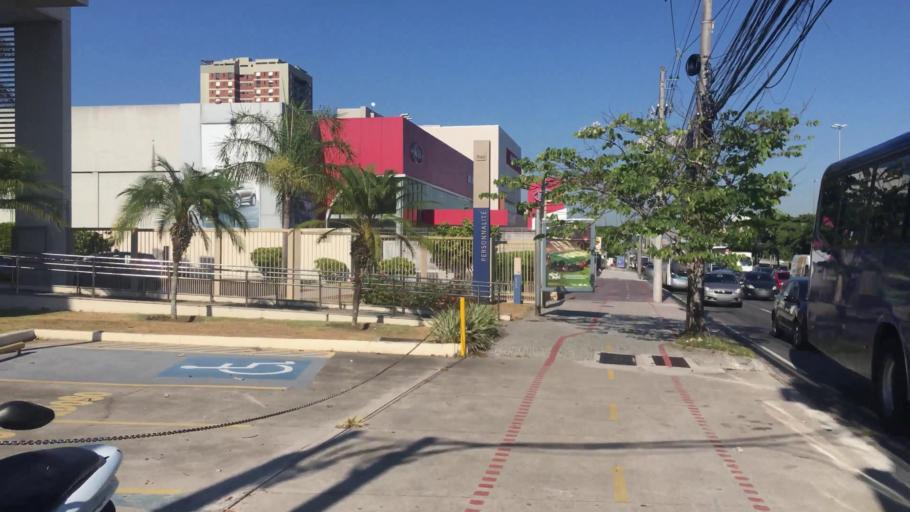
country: BR
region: Rio de Janeiro
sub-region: Rio De Janeiro
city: Rio de Janeiro
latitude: -23.0004
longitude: -43.3562
